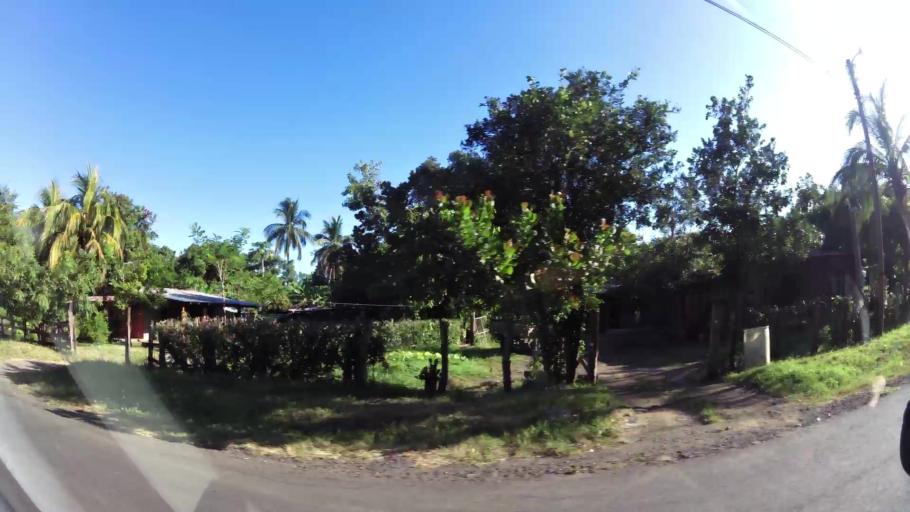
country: CR
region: Guanacaste
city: Sardinal
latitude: 10.4886
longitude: -85.6244
